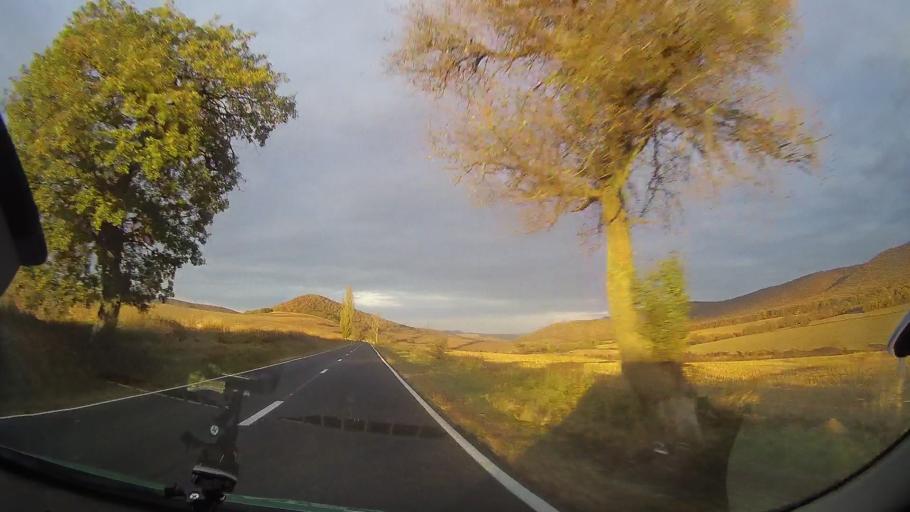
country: RO
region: Tulcea
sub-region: Comuna Ciucurova
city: Ciucurova
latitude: 44.9411
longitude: 28.4934
